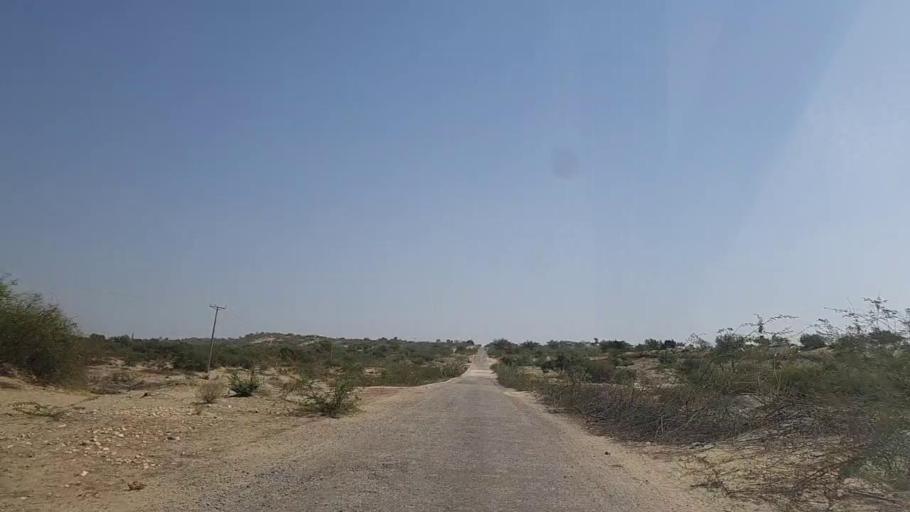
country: PK
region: Sindh
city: Diplo
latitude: 24.5151
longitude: 69.3759
